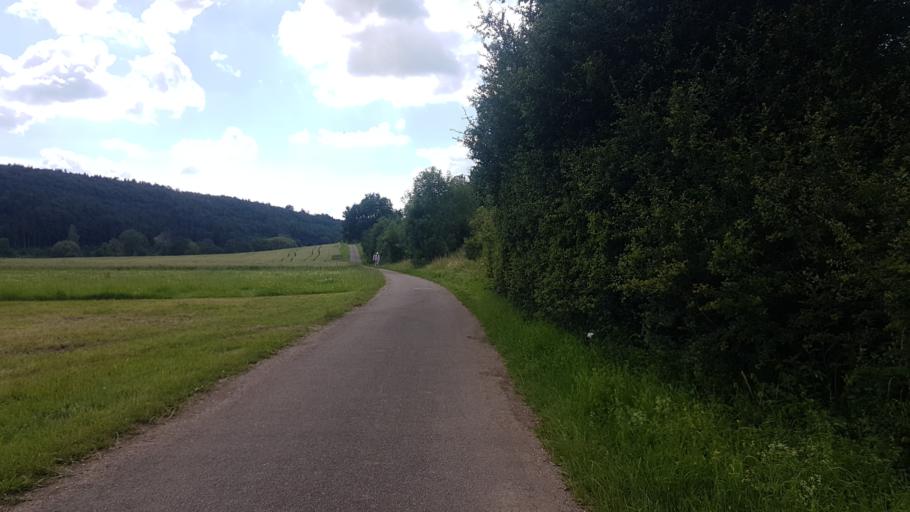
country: DE
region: Bavaria
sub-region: Regierungsbezirk Mittelfranken
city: Pappenheim
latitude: 48.9367
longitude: 10.9440
